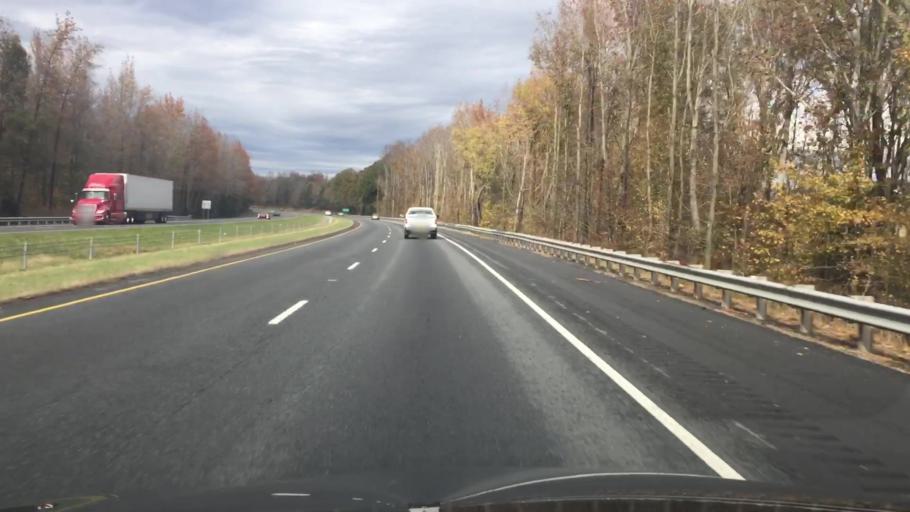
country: US
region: North Carolina
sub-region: Rockingham County
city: Reidsville
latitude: 36.2718
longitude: -79.6416
